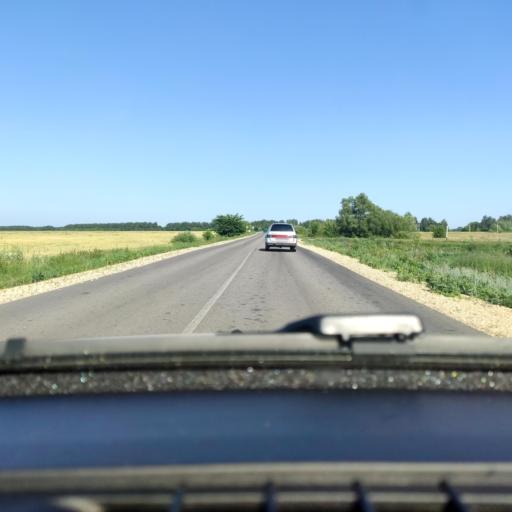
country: RU
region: Voronezj
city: Pereleshinskiy
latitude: 51.6294
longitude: 40.3300
